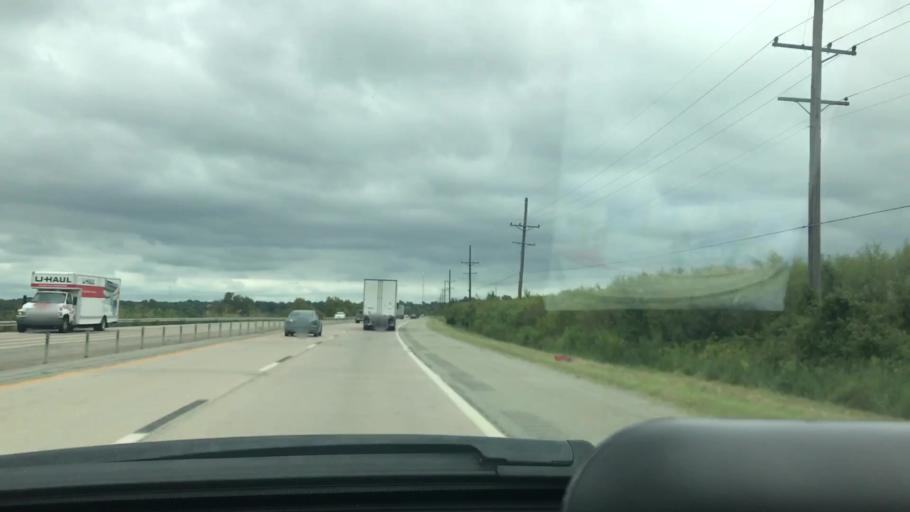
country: US
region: Oklahoma
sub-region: McIntosh County
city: Eufaula
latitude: 35.3416
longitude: -95.5844
